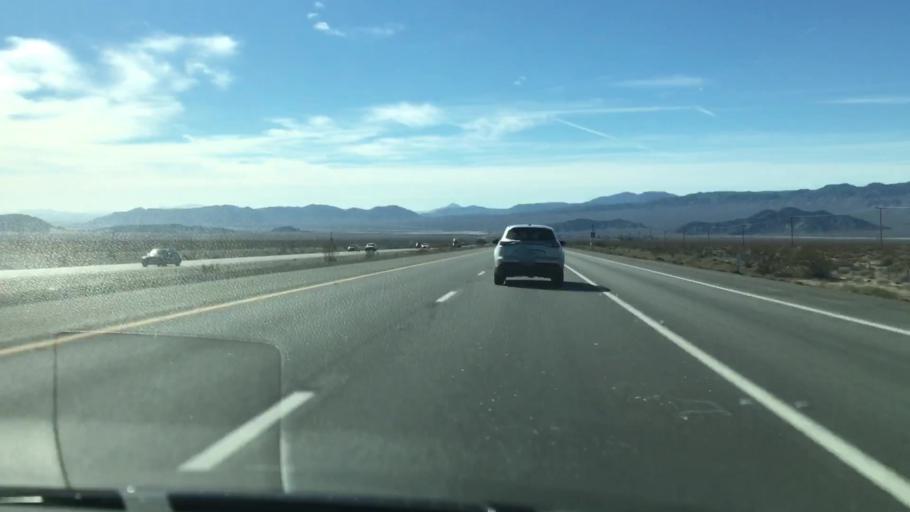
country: US
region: Nevada
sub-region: Clark County
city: Sandy Valley
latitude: 35.3089
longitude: -116.0069
